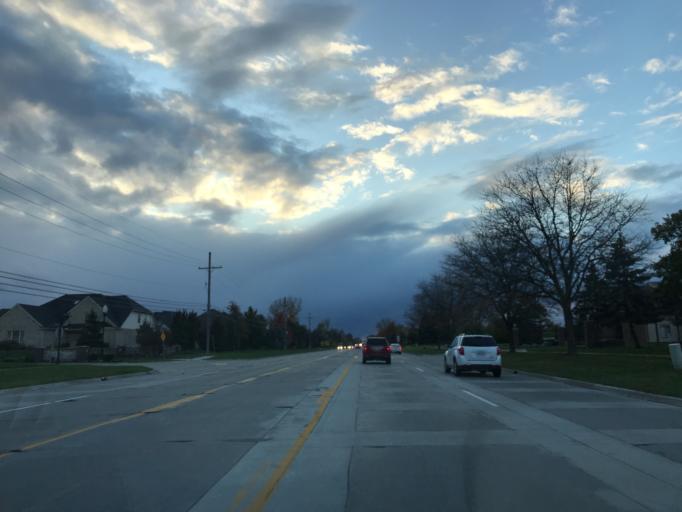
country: US
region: Michigan
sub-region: Oakland County
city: Farmington
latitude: 42.4403
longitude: -83.3880
